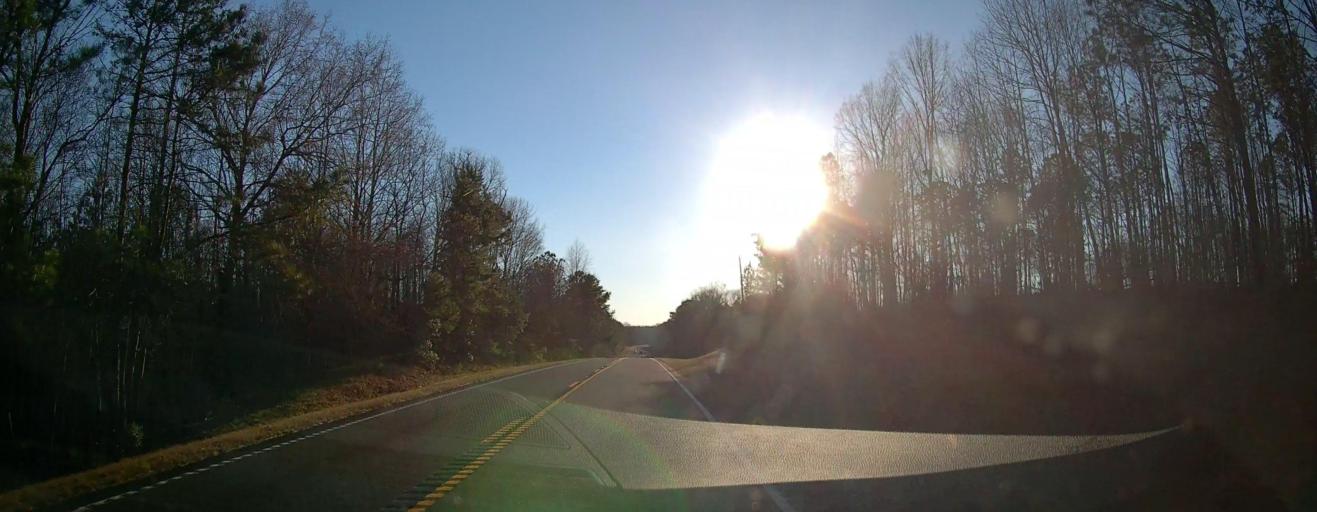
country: US
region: Georgia
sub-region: Talbot County
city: Talbotton
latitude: 32.6610
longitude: -84.6367
